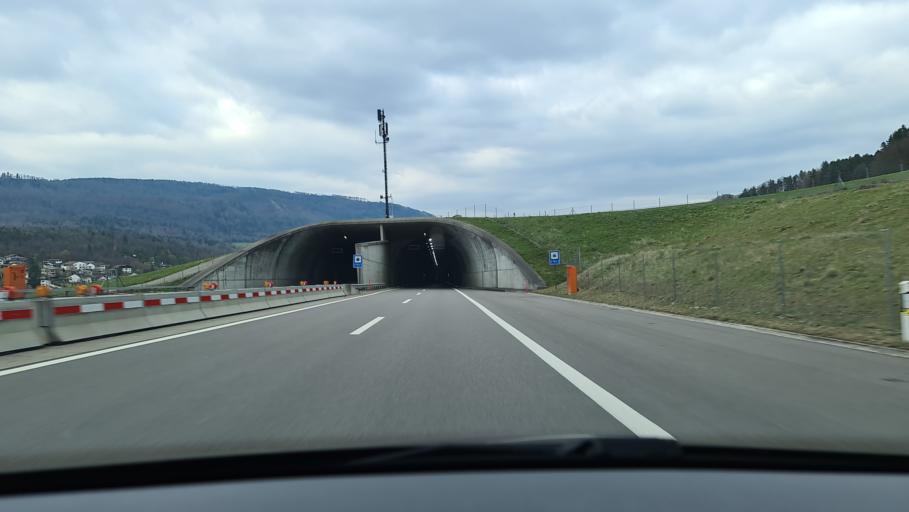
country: CH
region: Jura
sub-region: Delemont District
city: Courfaivre
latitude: 47.3506
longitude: 7.2904
